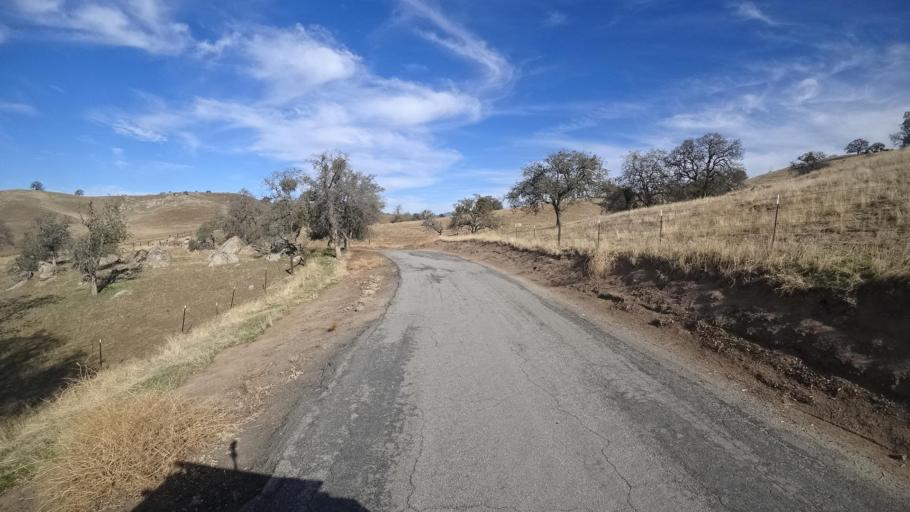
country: US
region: California
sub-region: Kern County
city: Oildale
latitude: 35.6073
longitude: -118.8260
